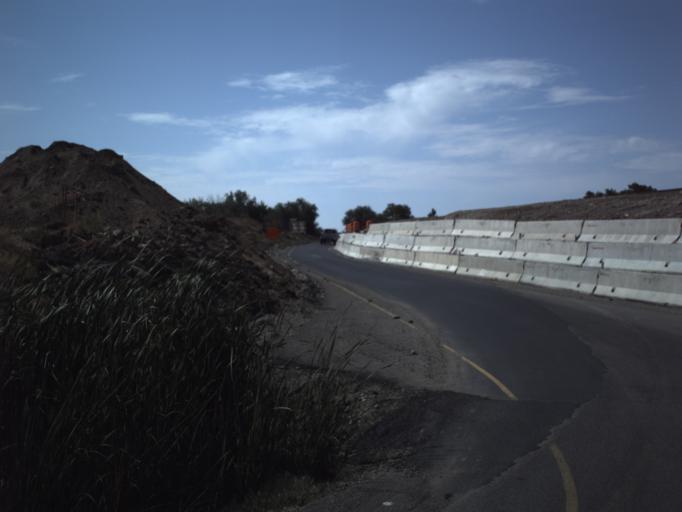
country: US
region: Utah
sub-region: Davis County
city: Clearfield
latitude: 41.1039
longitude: -112.0027
